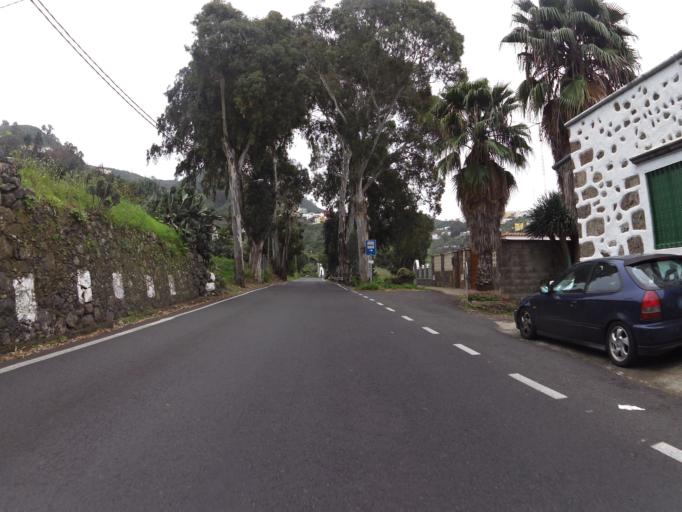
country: ES
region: Canary Islands
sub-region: Provincia de Las Palmas
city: Teror
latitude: 28.0712
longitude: -15.5243
